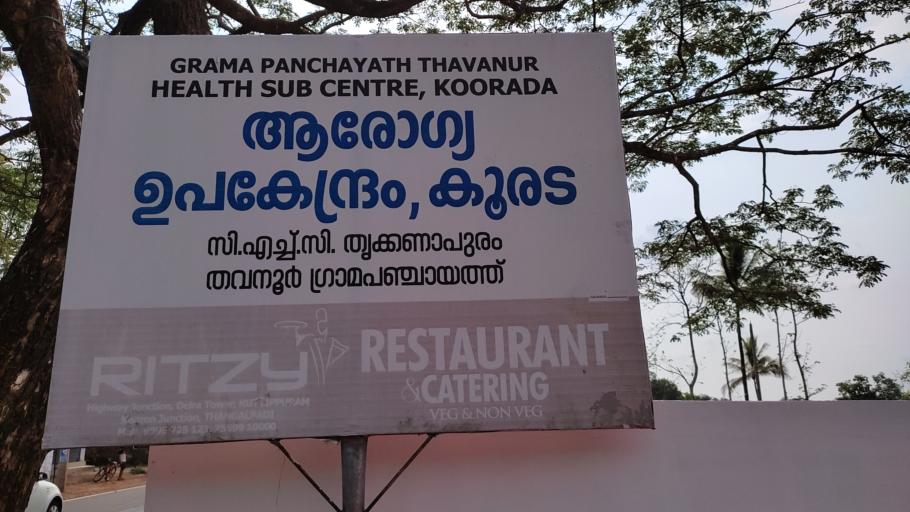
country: IN
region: Kerala
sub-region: Malappuram
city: Ponnani
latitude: 10.8385
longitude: 76.0112
